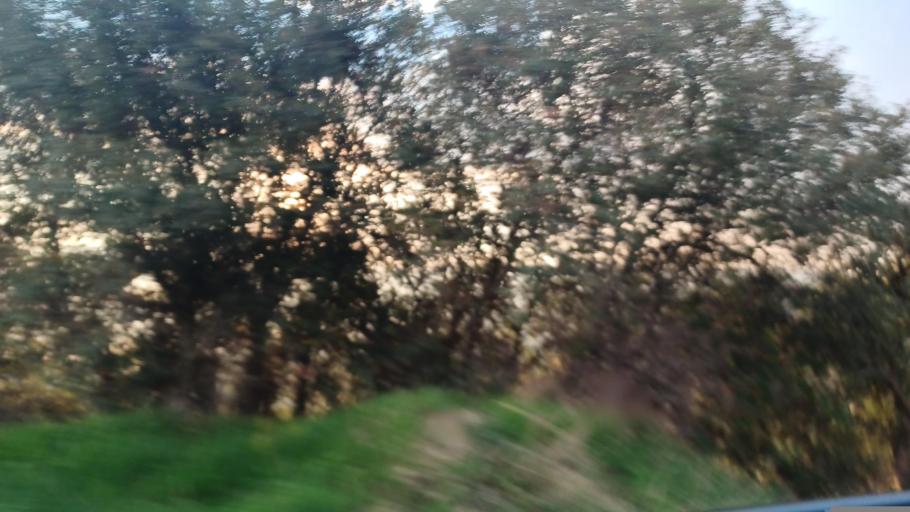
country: CY
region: Pafos
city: Mesogi
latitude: 34.8403
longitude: 32.5253
